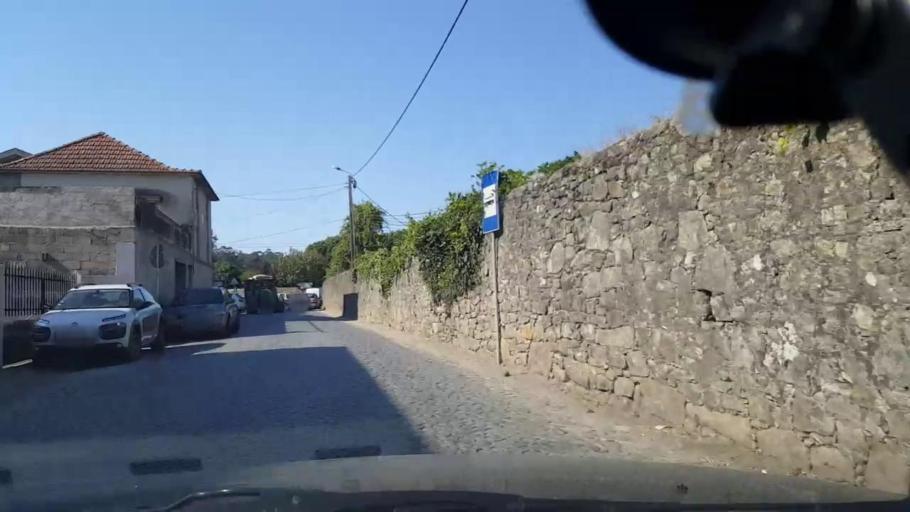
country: PT
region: Porto
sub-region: Vila do Conde
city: Arvore
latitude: 41.3931
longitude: -8.6912
